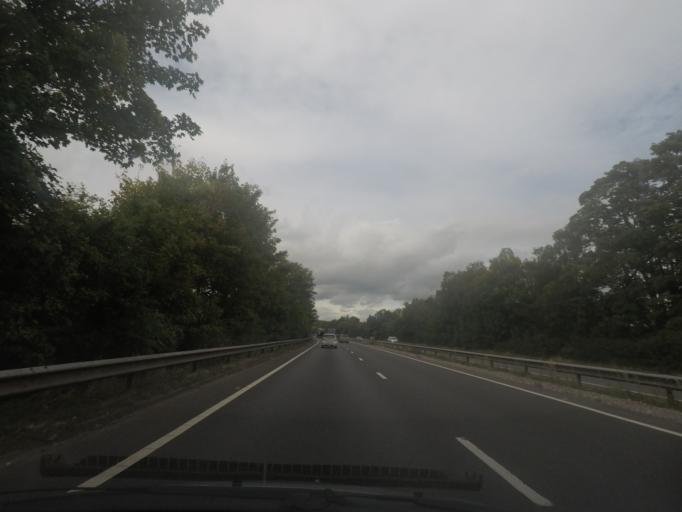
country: GB
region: England
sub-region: Hampshire
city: Overton
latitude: 51.2576
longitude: -1.3393
